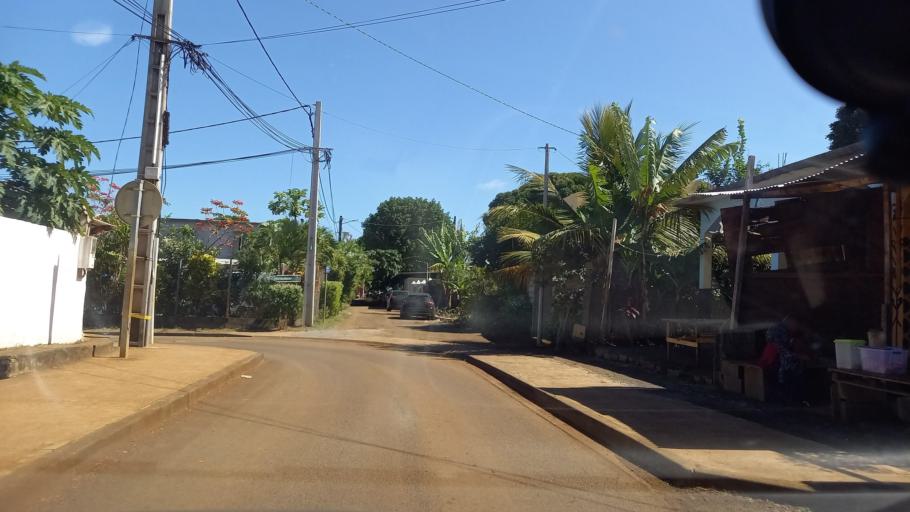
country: YT
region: Tsingoni
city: Tsingoni
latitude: -12.7885
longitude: 45.1355
